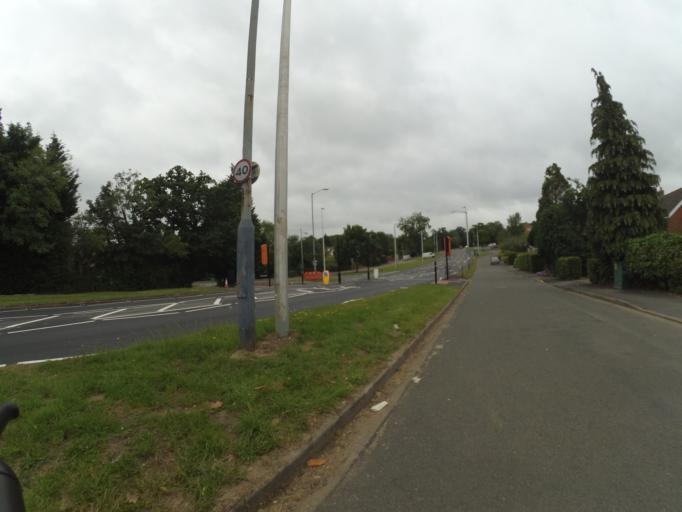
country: GB
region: England
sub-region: Warwickshire
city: Rugby
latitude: 52.3546
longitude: -1.2713
